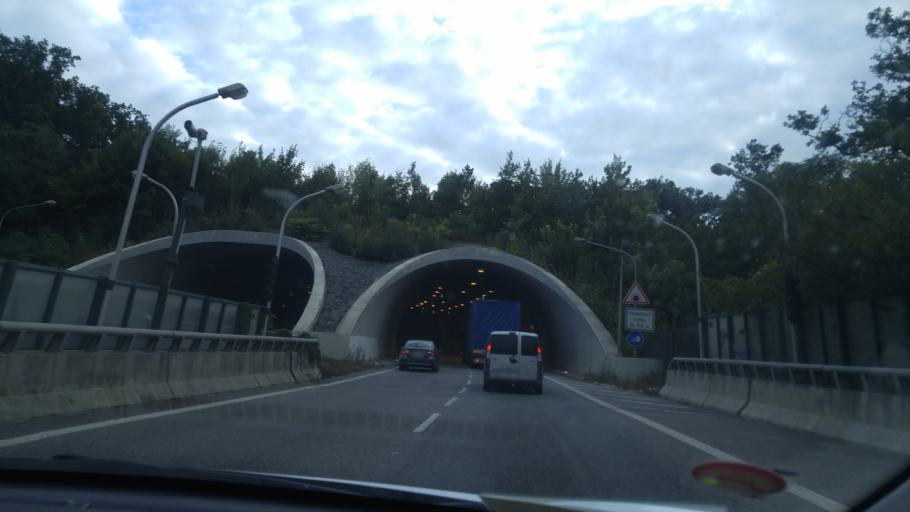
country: CZ
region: South Moravian
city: Ostopovice
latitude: 49.1885
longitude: 16.5671
